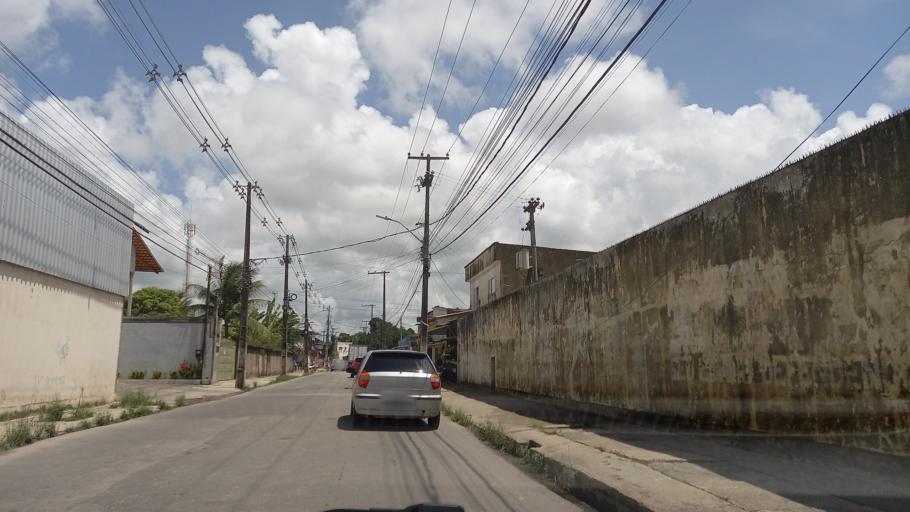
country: BR
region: Pernambuco
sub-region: Jaboatao Dos Guararapes
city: Jaboatao
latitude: -8.2215
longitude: -34.9602
